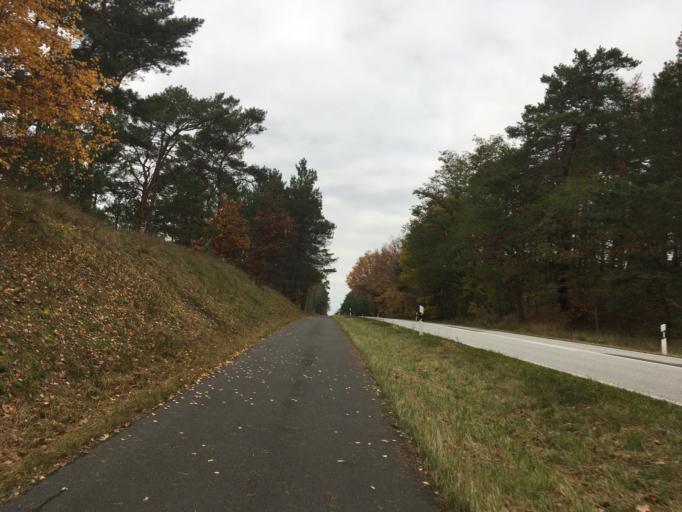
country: DE
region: Brandenburg
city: Mixdorf
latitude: 52.1949
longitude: 14.4616
